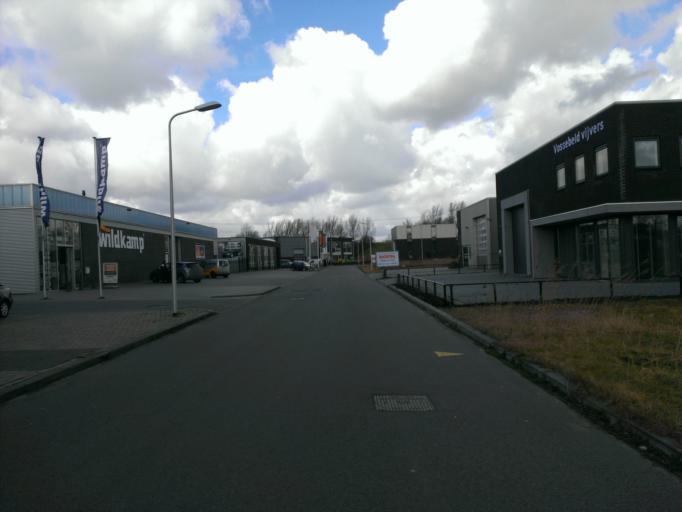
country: NL
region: Drenthe
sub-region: Gemeente Hoogeveen
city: Hoogeveen
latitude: 52.7379
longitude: 6.4812
